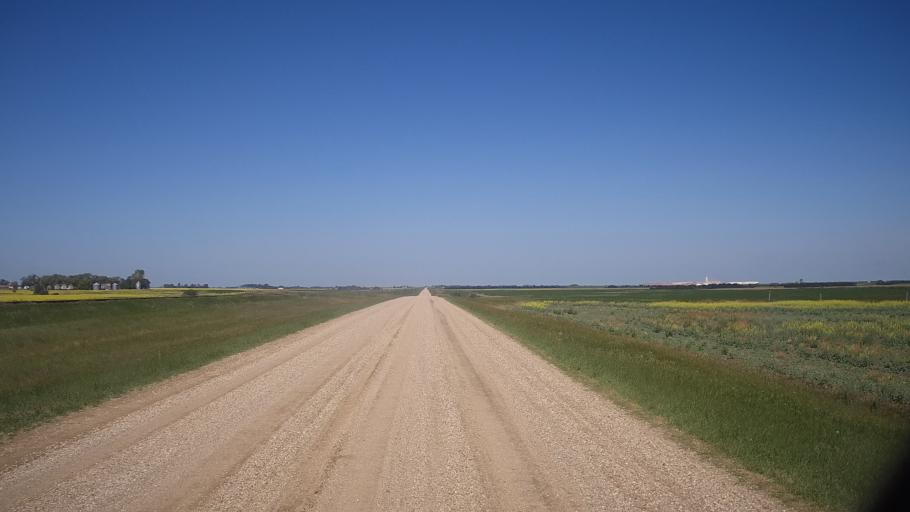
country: CA
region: Saskatchewan
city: Watrous
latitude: 51.8664
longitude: -105.9802
